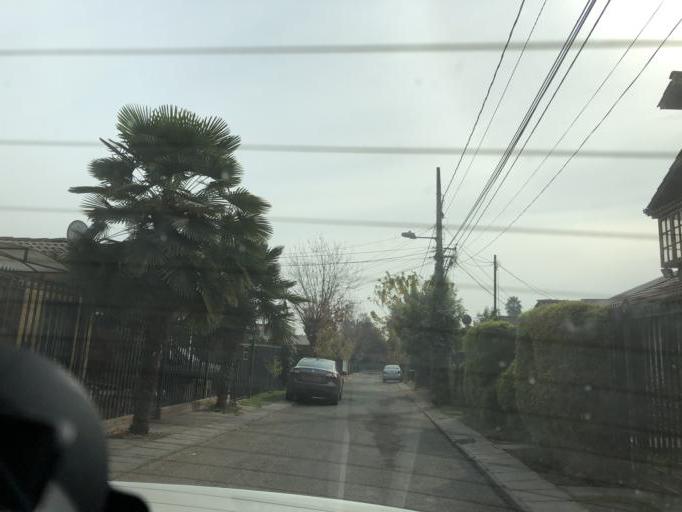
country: CL
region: Santiago Metropolitan
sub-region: Provincia de Cordillera
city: Puente Alto
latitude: -33.5505
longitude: -70.5571
